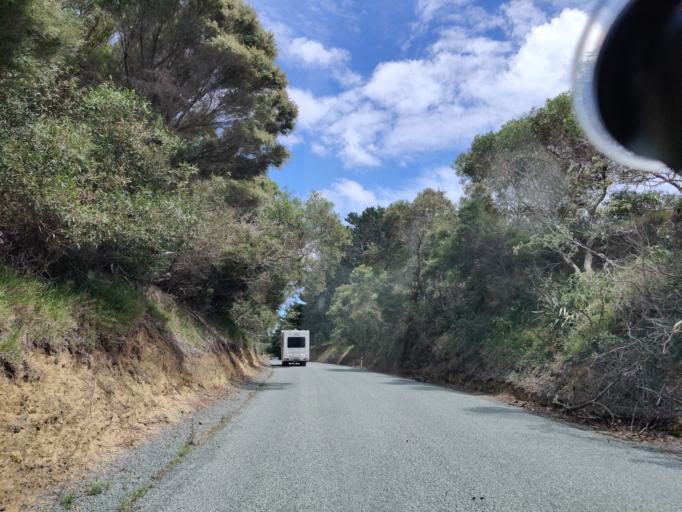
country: NZ
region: Northland
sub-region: Far North District
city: Kaitaia
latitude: -34.7697
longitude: 173.0832
